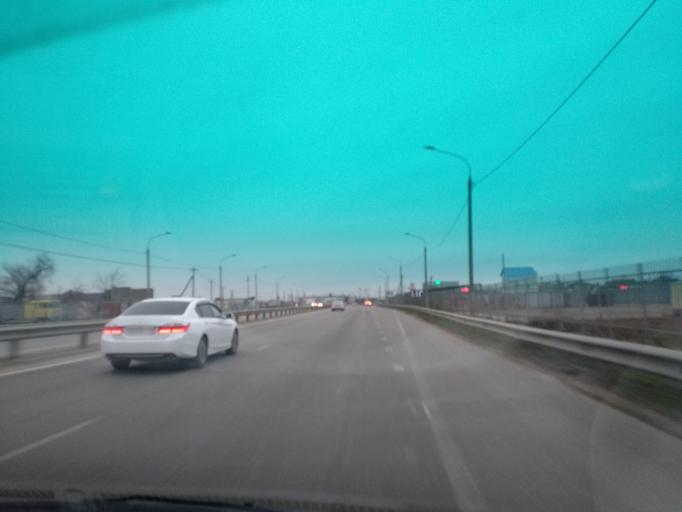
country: RU
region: Krasnodarskiy
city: Pashkovskiy
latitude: 45.0606
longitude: 39.1333
